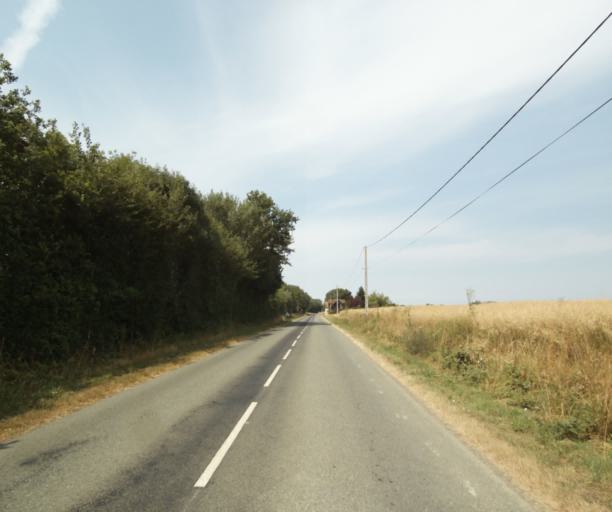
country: FR
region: Centre
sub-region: Departement d'Eure-et-Loir
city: La Bazoche-Gouet
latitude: 48.1729
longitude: 0.9922
